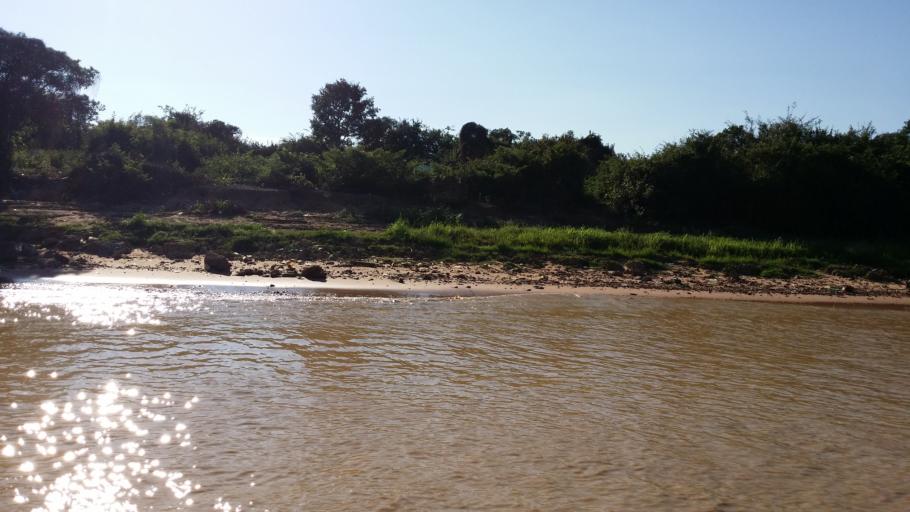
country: KH
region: Siem Reap
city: Siem Reap
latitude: 13.2537
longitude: 103.8229
